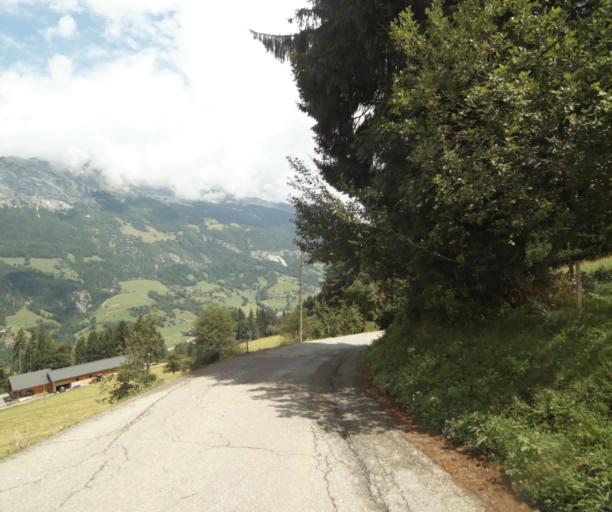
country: FR
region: Rhone-Alpes
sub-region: Departement de la Haute-Savoie
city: Thones
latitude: 45.8944
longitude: 6.3639
